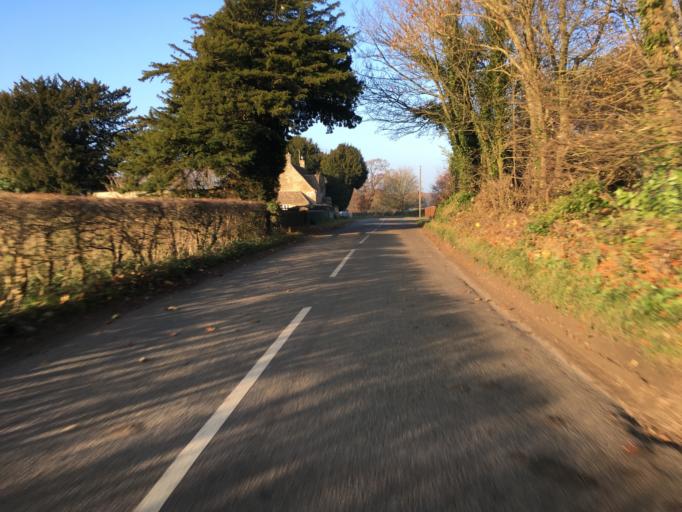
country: GB
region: England
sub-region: Wiltshire
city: Luckington
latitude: 51.5610
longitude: -2.2877
